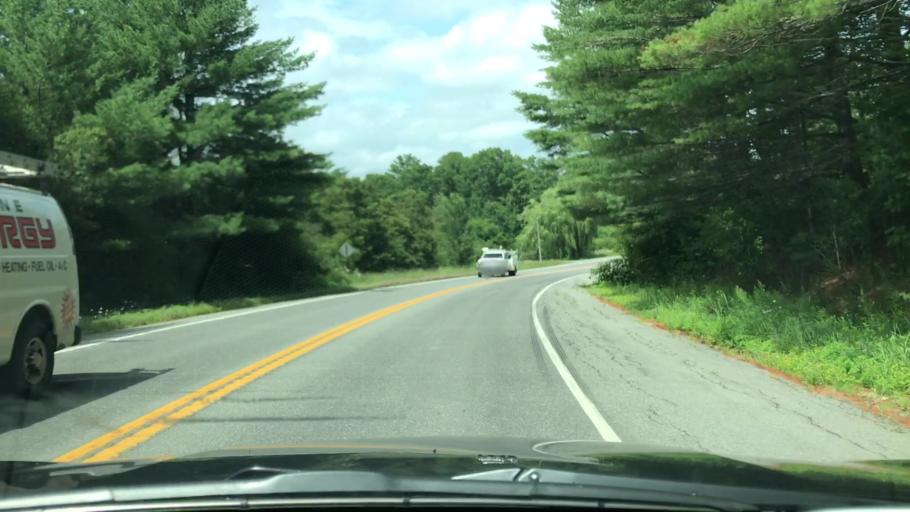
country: US
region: Maine
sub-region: Waldo County
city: Belfast
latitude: 44.3913
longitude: -68.9908
